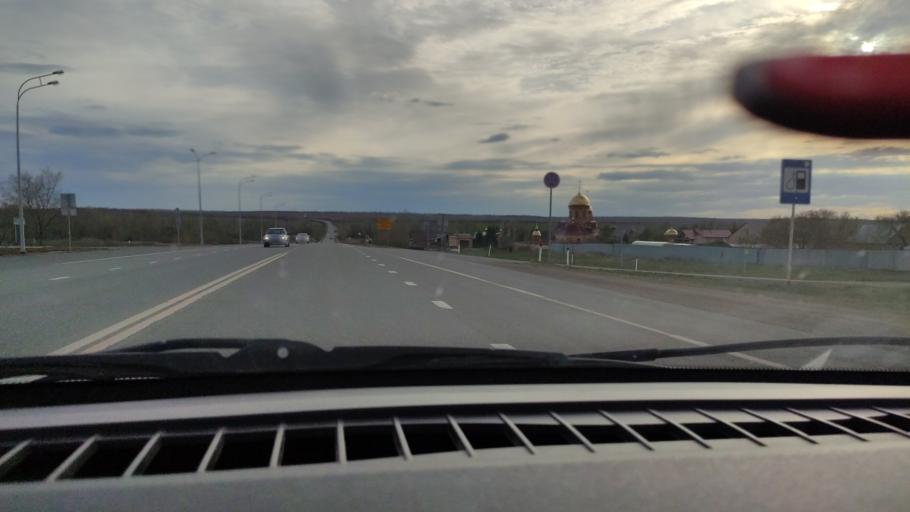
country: RU
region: Orenburg
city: Tatarskaya Kargala
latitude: 52.0266
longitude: 55.2289
